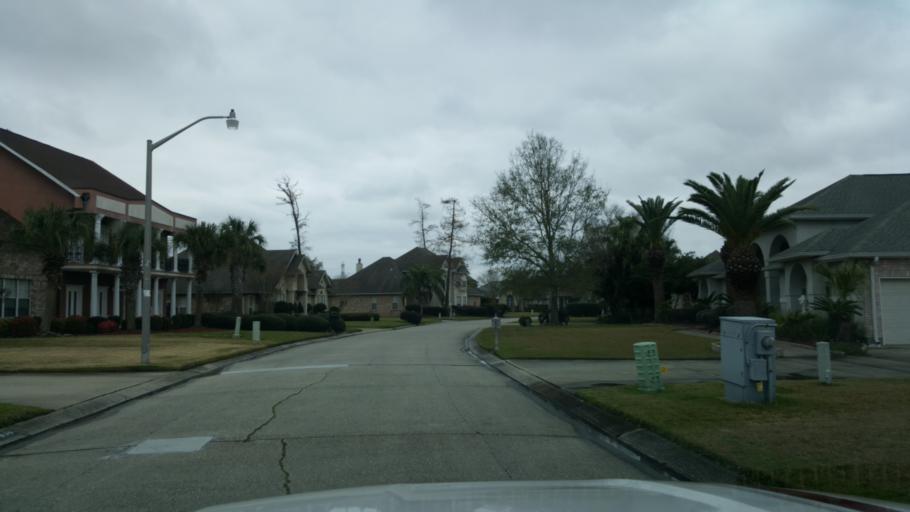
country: US
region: Louisiana
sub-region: Jefferson Parish
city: Woodmere
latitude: 29.8757
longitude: -90.0811
